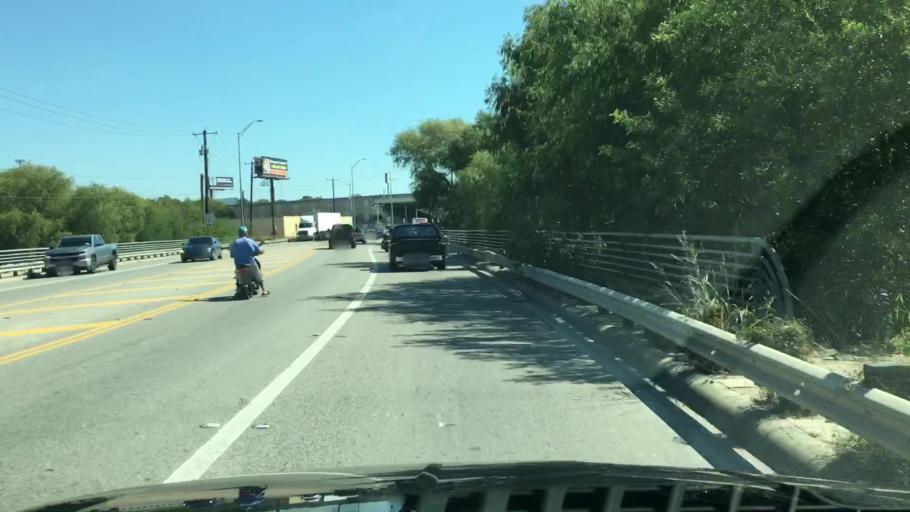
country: US
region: Texas
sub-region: Bexar County
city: Windcrest
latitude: 29.5343
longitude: -98.3921
